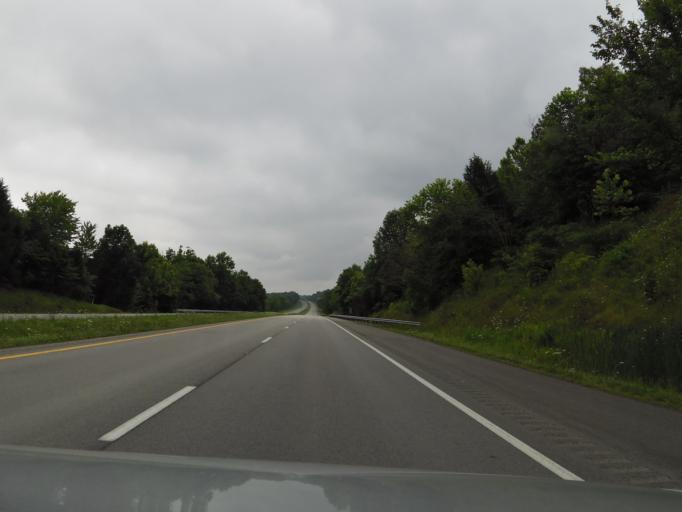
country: US
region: Kentucky
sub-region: Grayson County
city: Leitchfield
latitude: 37.4113
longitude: -86.4362
